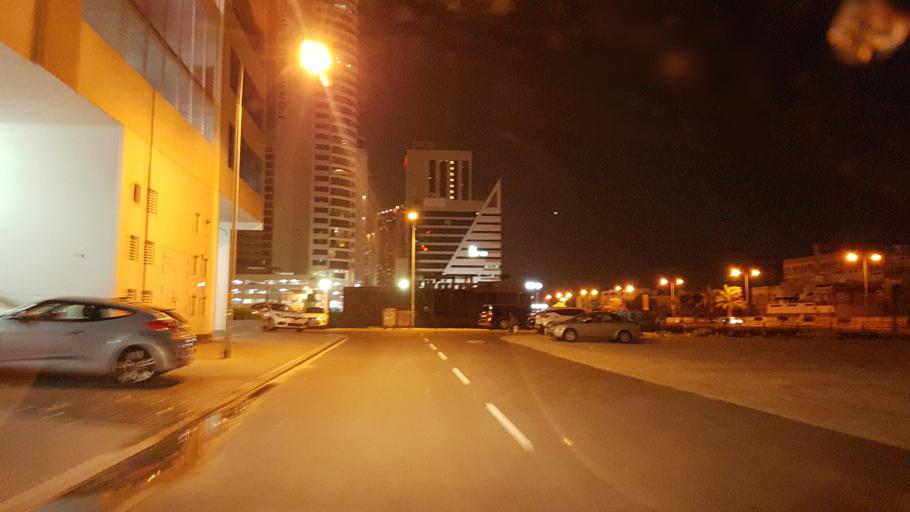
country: BH
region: Manama
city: Jidd Hafs
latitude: 26.2297
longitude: 50.5474
